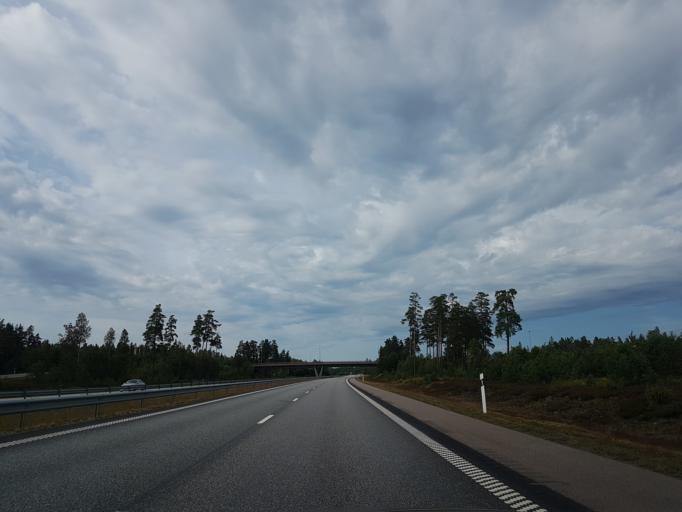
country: SE
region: Joenkoeping
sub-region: Vaggeryds Kommun
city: Skillingaryd
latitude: 57.3434
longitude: 14.1030
